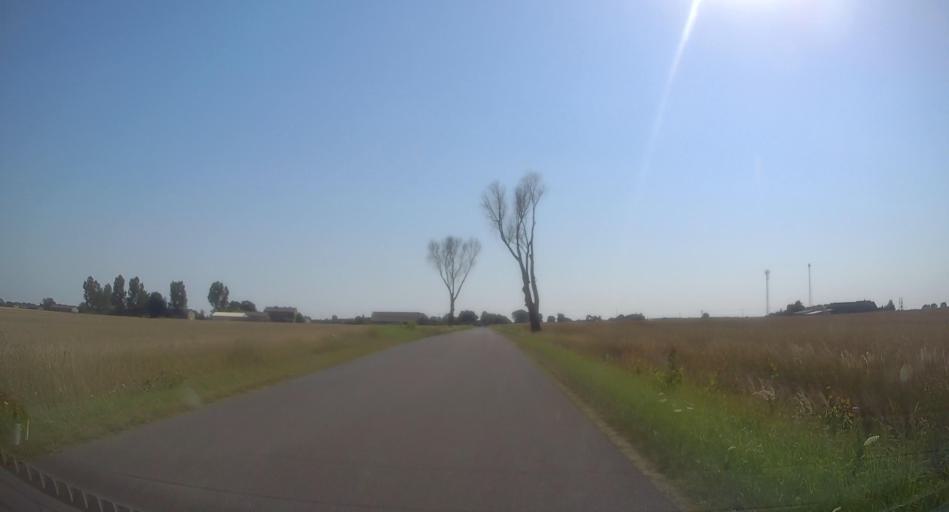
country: PL
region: Lodz Voivodeship
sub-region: Powiat skierniewicki
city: Kaweczyn Nowy
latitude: 51.8817
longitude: 20.2191
